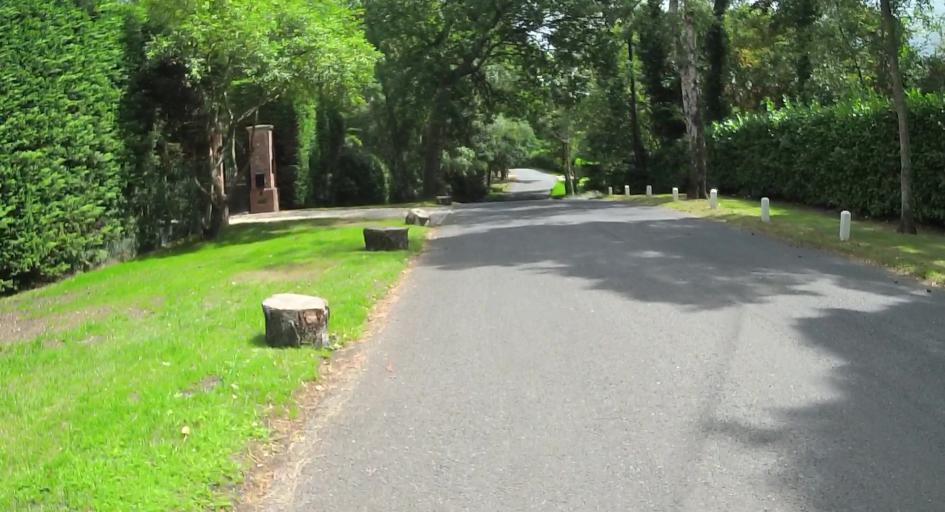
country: GB
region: England
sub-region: Surrey
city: Seale
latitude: 51.2113
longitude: -0.7551
